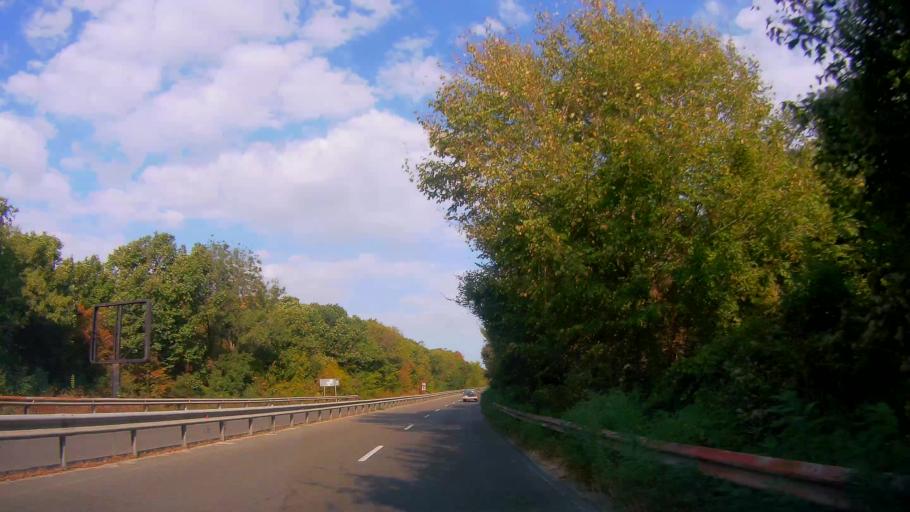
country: BG
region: Burgas
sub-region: Obshtina Burgas
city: Burgas
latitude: 42.4305
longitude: 27.5328
